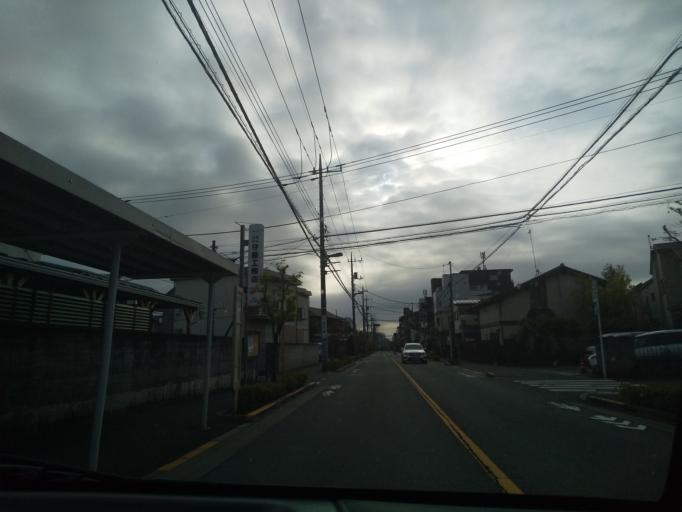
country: JP
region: Tokyo
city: Kokubunji
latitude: 35.7021
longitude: 139.4923
